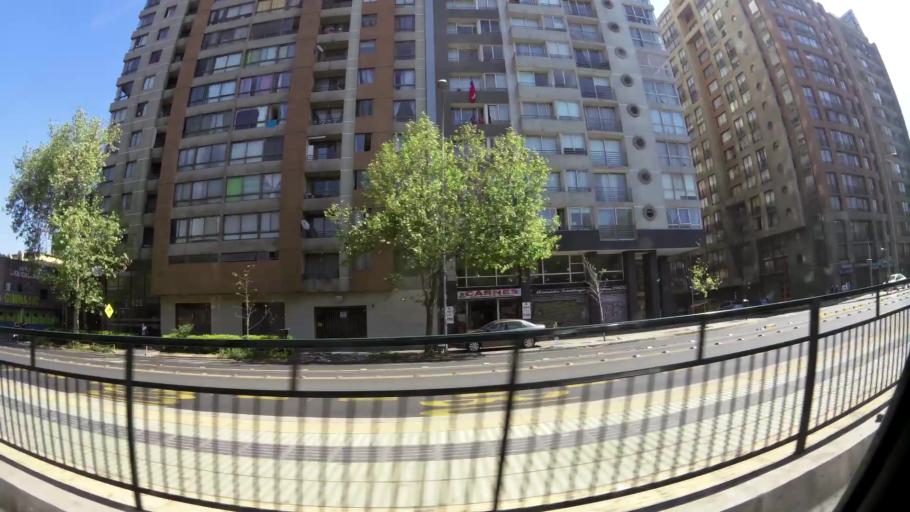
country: CL
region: Santiago Metropolitan
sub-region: Provincia de Santiago
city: Santiago
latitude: -33.4490
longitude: -70.6318
